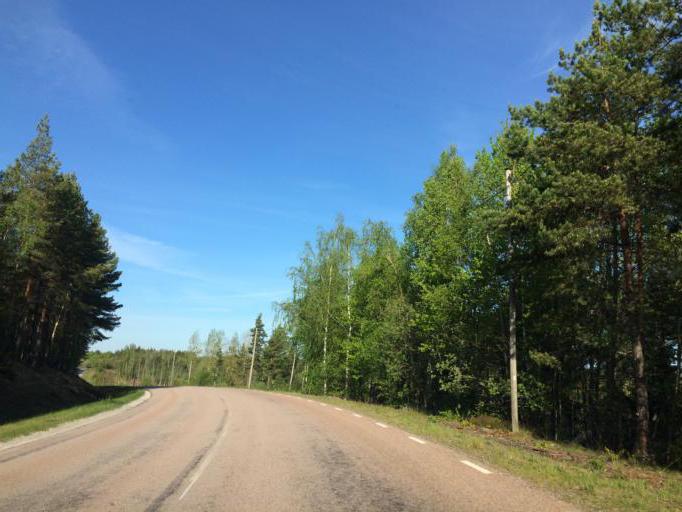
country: SE
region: Soedermanland
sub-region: Eskilstuna Kommun
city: Kvicksund
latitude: 59.4223
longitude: 16.3009
